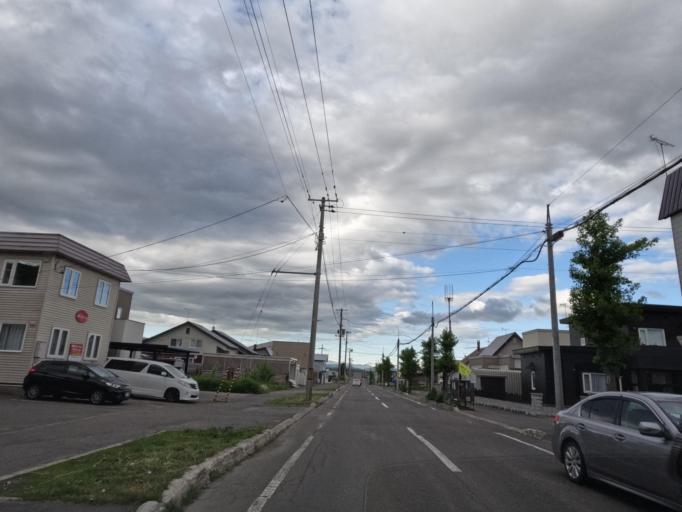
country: JP
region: Hokkaido
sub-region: Asahikawa-shi
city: Asahikawa
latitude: 43.7731
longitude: 142.3126
